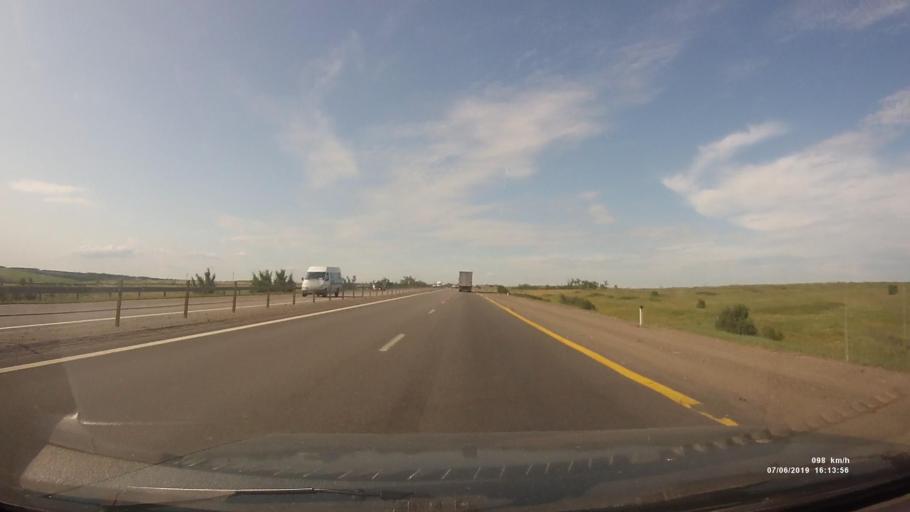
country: RU
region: Rostov
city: Likhoy
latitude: 48.1518
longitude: 40.2610
